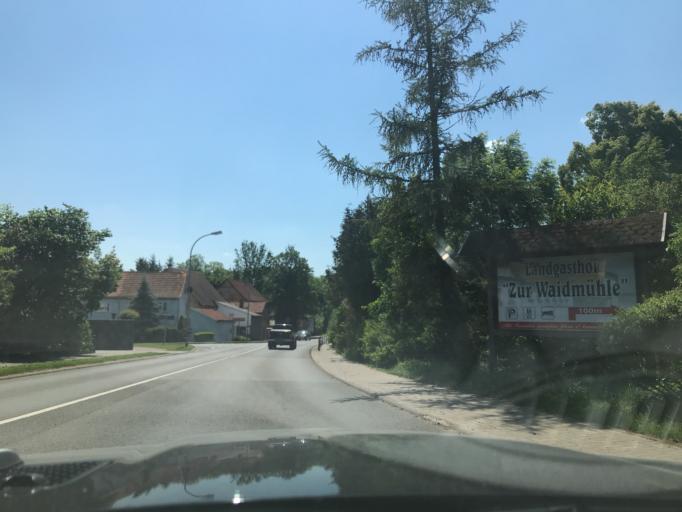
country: DE
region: Thuringia
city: Westhausen
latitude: 51.0146
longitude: 10.6842
